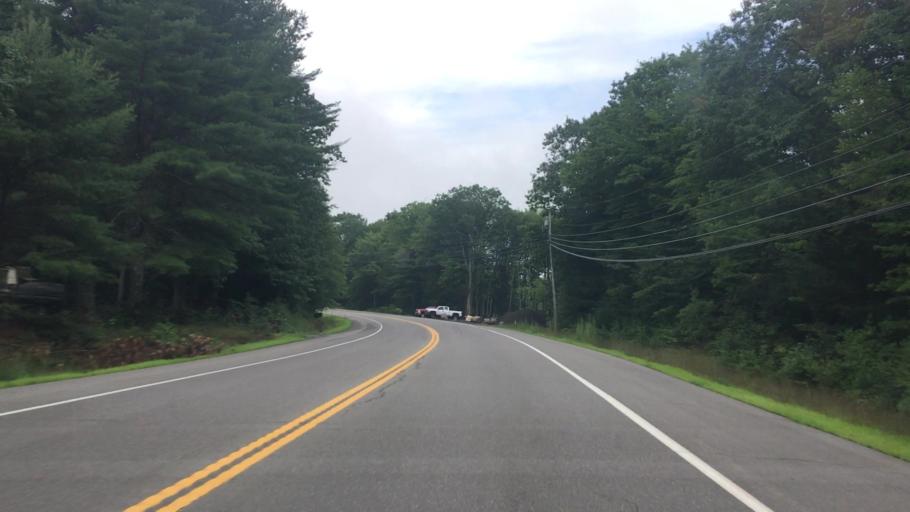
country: US
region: Maine
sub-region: York County
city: Sanford (historical)
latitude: 43.4286
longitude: -70.8088
